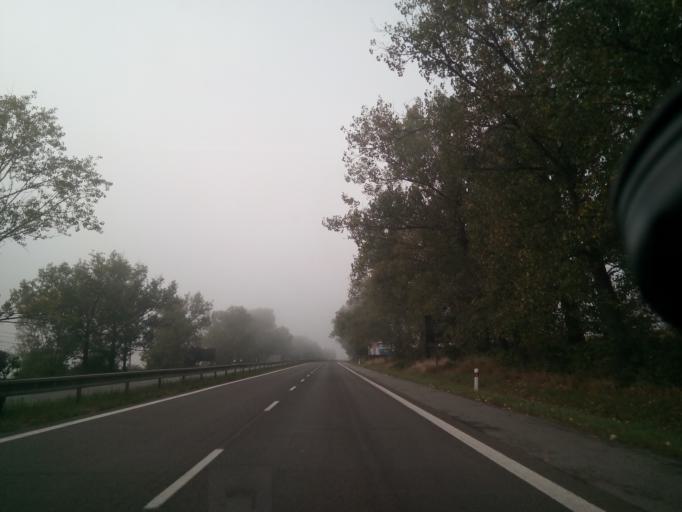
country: SK
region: Kosicky
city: Kosice
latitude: 48.6762
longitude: 21.2132
